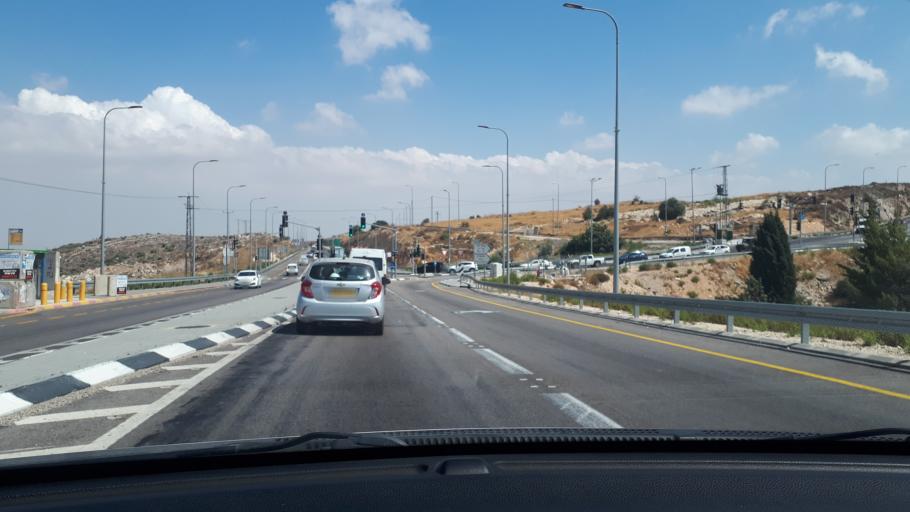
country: PS
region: West Bank
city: Burqah
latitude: 31.9121
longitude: 35.2497
